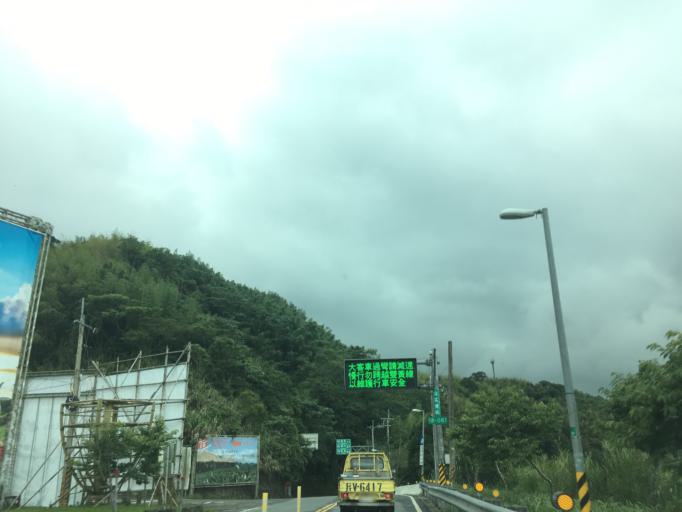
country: TW
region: Taiwan
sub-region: Chiayi
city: Jiayi Shi
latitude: 23.4633
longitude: 120.6893
